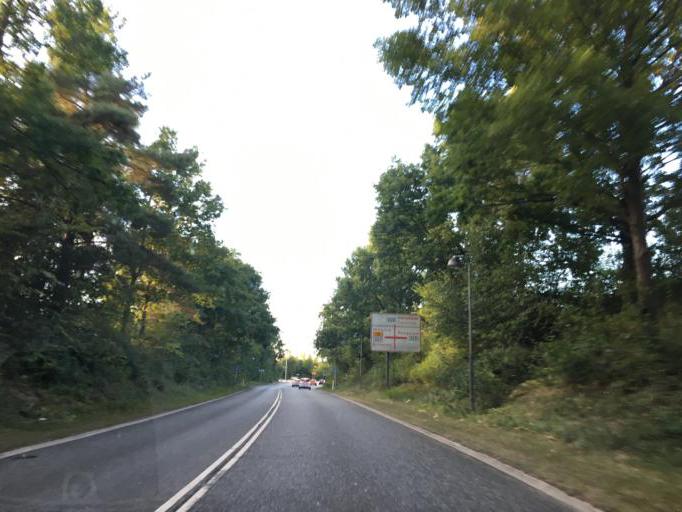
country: DK
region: Capital Region
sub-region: Horsholm Kommune
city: Horsholm
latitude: 55.8764
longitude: 12.4961
